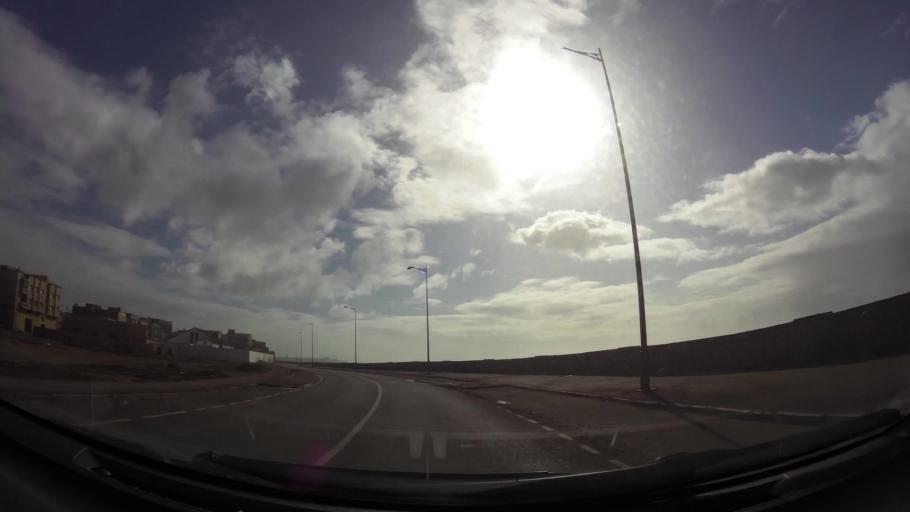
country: MA
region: Doukkala-Abda
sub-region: El-Jadida
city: El Jadida
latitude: 33.2638
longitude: -8.5119
